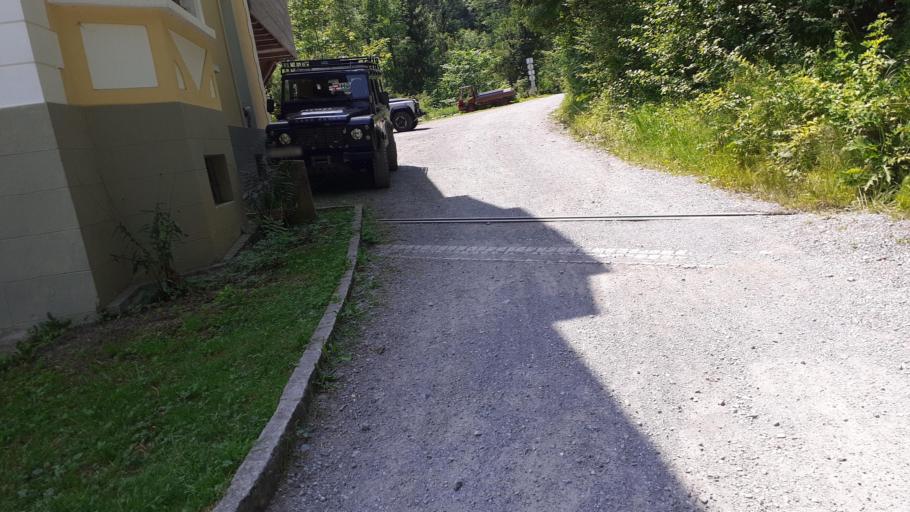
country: AT
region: Vorarlberg
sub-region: Politischer Bezirk Bregenz
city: Egg
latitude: 47.4468
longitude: 9.8900
